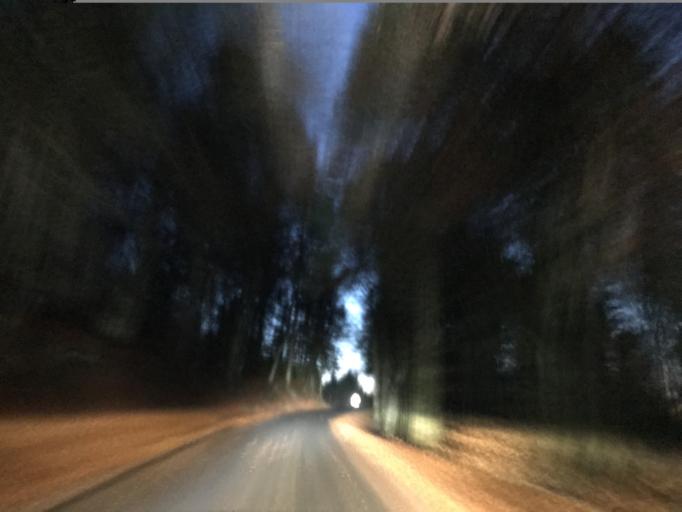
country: FR
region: Rhone-Alpes
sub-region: Departement de la Loire
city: Noiretable
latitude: 45.7332
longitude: 3.7385
